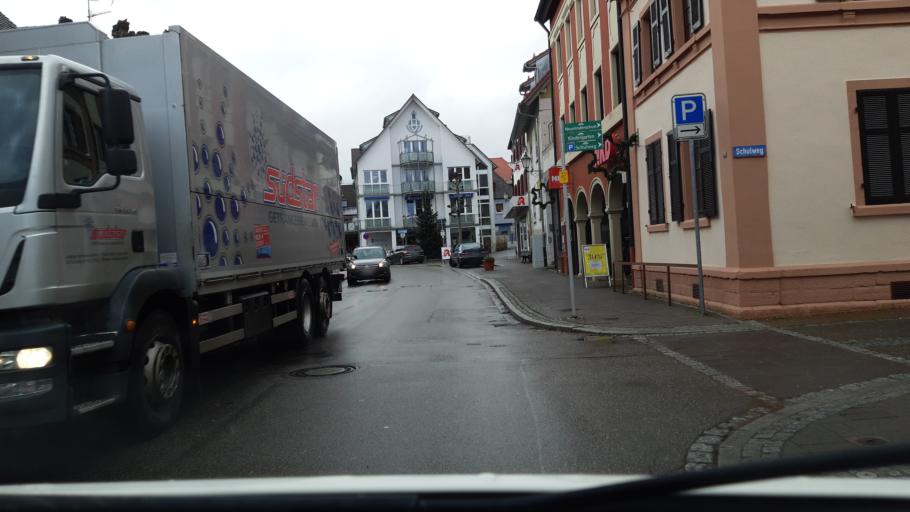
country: DE
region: Baden-Wuerttemberg
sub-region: Freiburg Region
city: Ihringen
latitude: 48.0445
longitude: 7.6470
